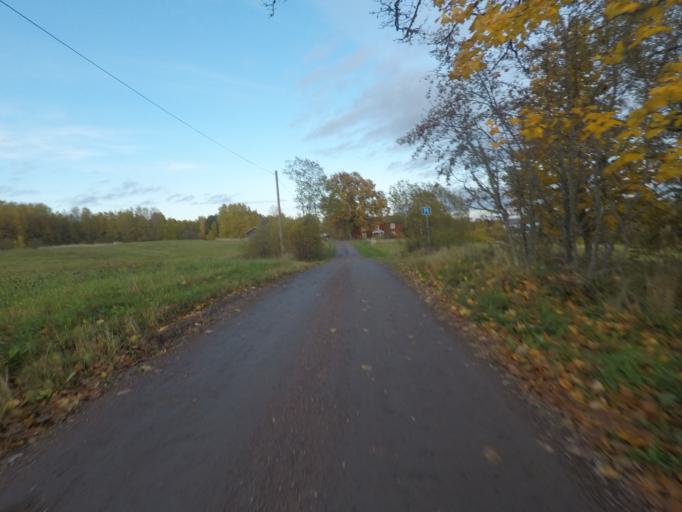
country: SE
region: OErebro
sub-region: Karlskoga Kommun
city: Karlskoga
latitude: 59.2957
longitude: 14.5060
